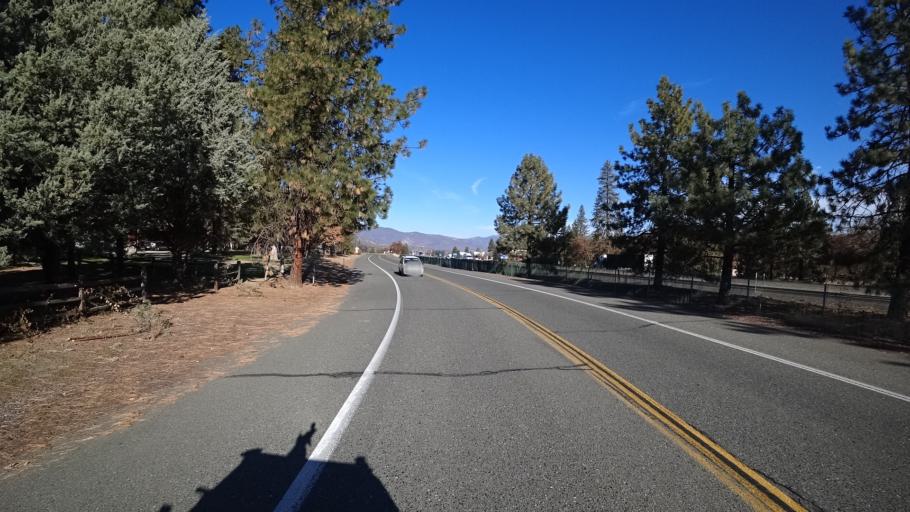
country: US
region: California
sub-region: Siskiyou County
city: Yreka
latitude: 41.6862
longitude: -122.6366
